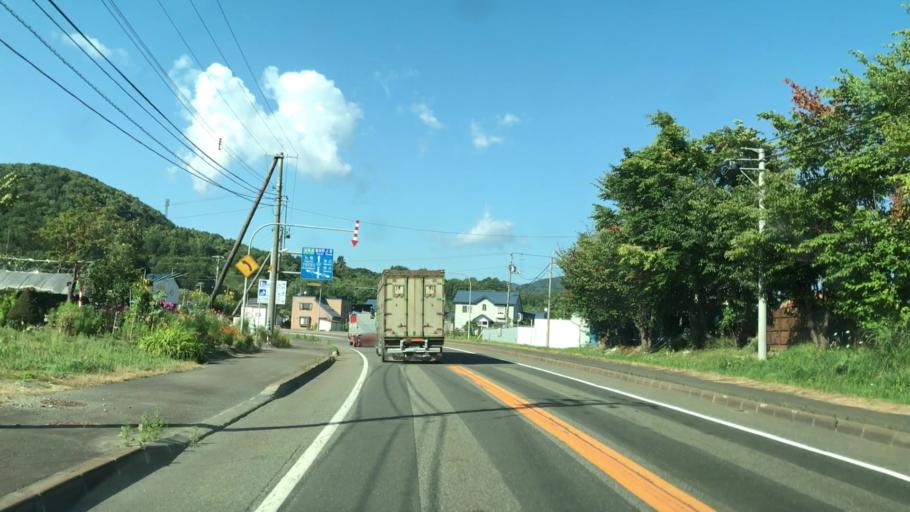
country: JP
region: Hokkaido
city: Shimo-furano
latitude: 42.8798
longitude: 142.4341
